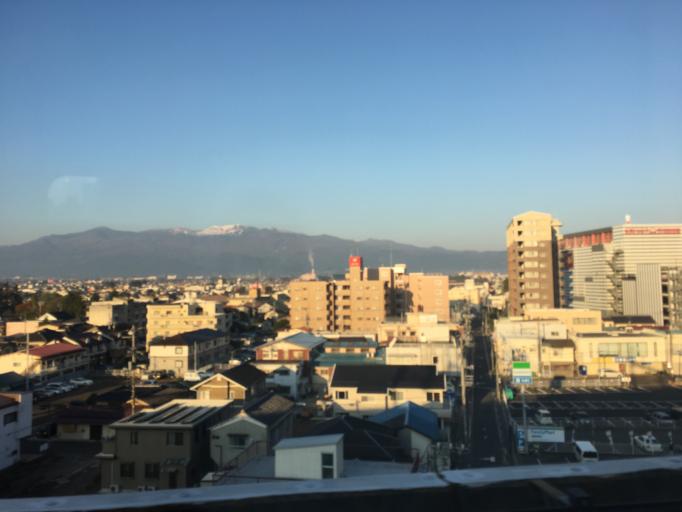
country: JP
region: Fukushima
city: Fukushima-shi
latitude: 37.7515
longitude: 140.4586
